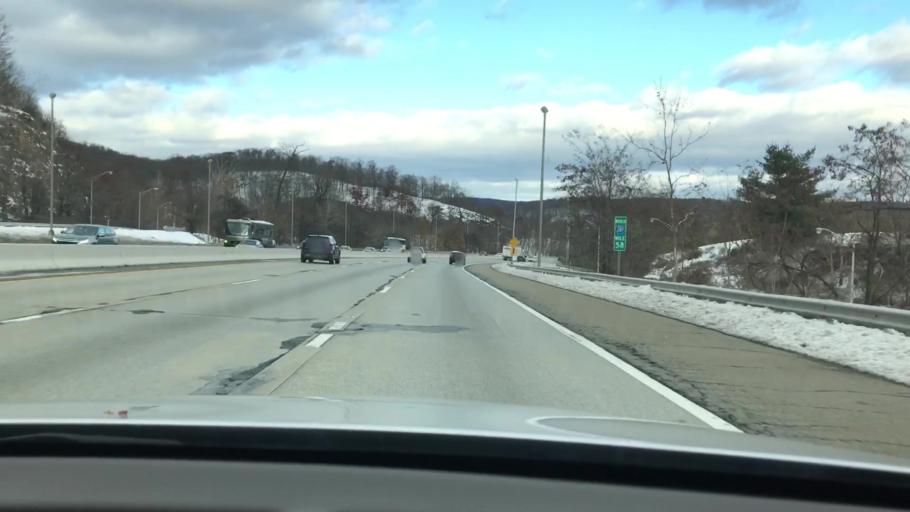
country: US
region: New Jersey
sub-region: Bergen County
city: Oakland
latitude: 41.0273
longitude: -74.2544
